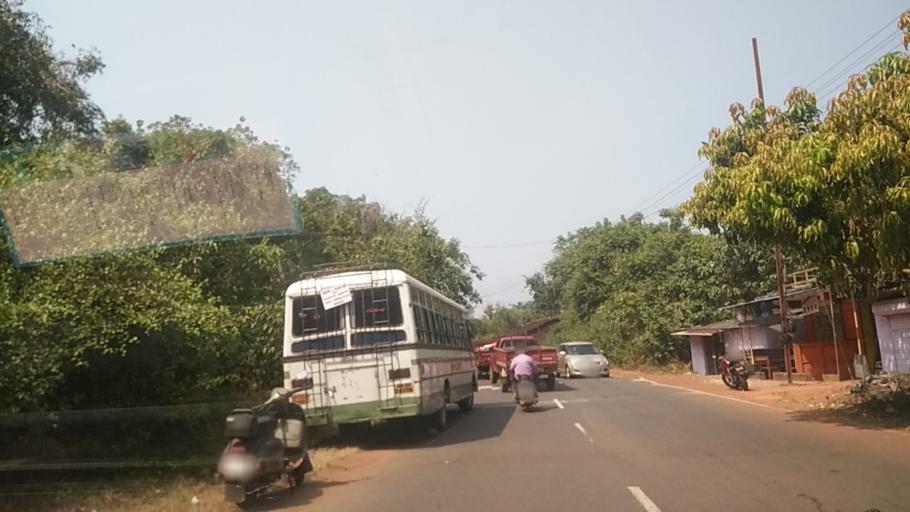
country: IN
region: Goa
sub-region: North Goa
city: Morjim
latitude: 15.6598
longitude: 73.7428
